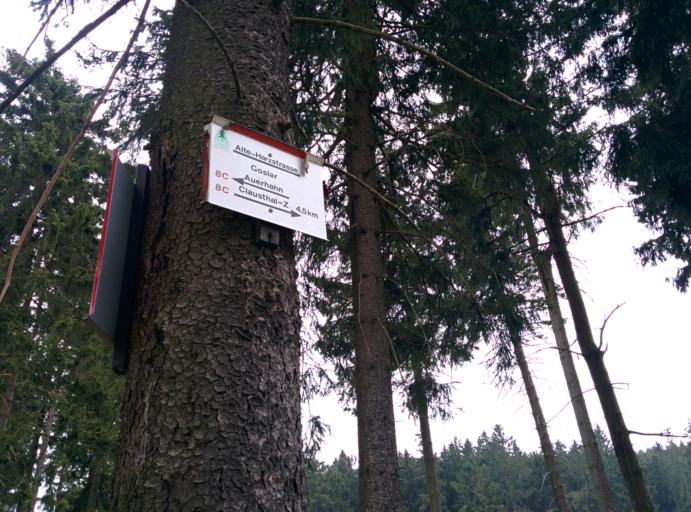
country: DE
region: Lower Saxony
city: Clausthal-Zellerfeld
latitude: 51.8540
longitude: 10.3654
